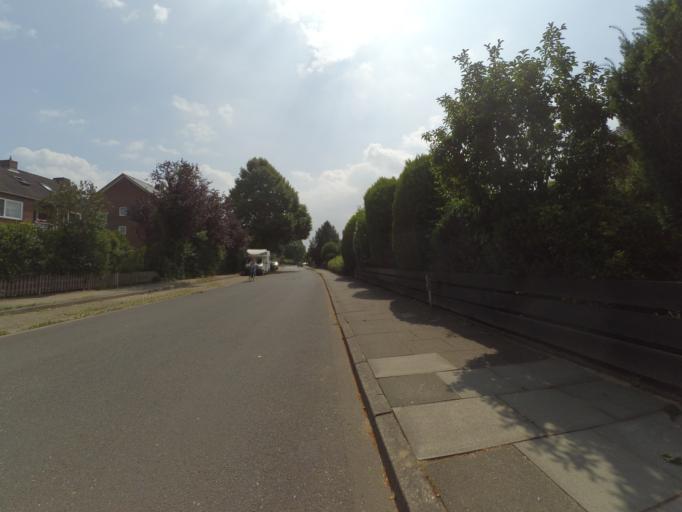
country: DE
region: Schleswig-Holstein
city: Bonningstedt
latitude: 53.6370
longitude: 9.9393
